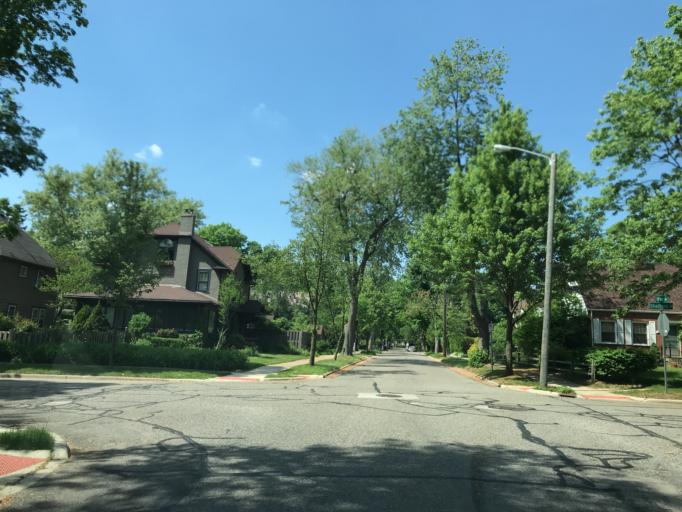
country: US
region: Michigan
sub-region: Washtenaw County
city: Ann Arbor
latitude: 42.2615
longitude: -83.7277
